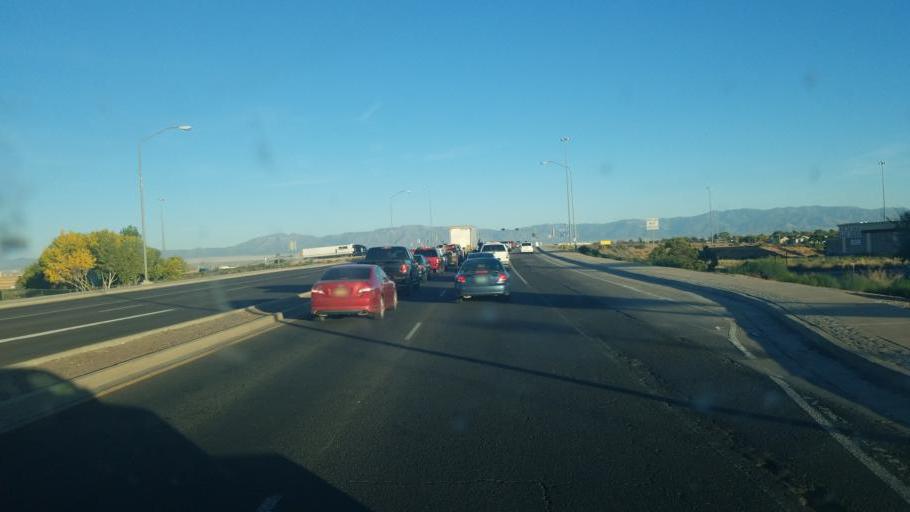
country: US
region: New Mexico
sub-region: Valencia County
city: Los Lunas
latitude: 34.8152
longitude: -106.7644
